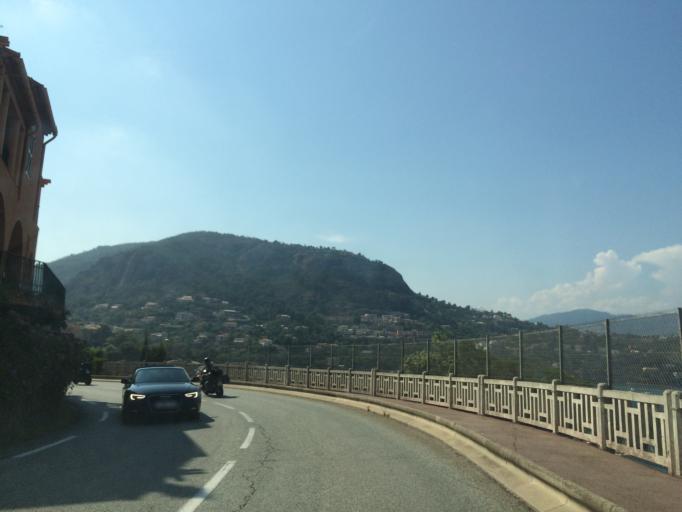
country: FR
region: Provence-Alpes-Cote d'Azur
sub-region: Departement des Alpes-Maritimes
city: Theoule-sur-Mer
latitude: 43.5063
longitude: 6.9436
